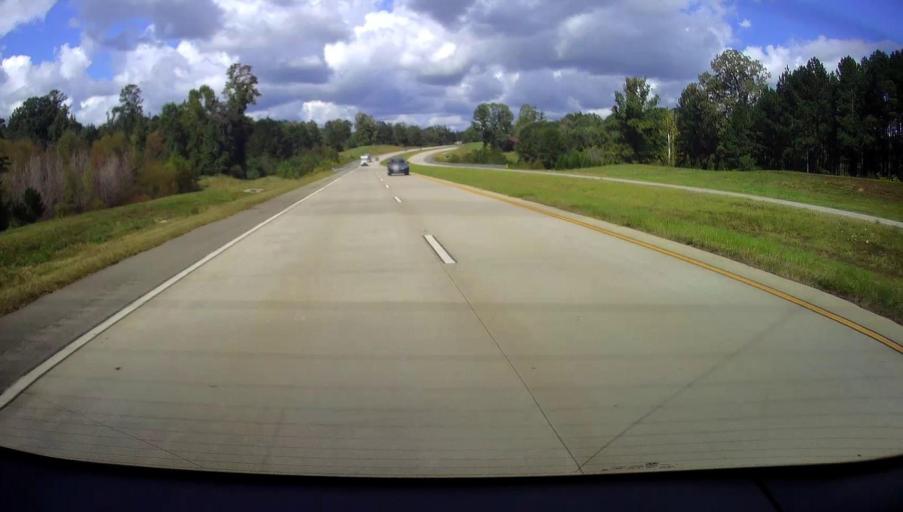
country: US
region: Georgia
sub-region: Jones County
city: Gray
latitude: 33.0049
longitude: -83.5739
